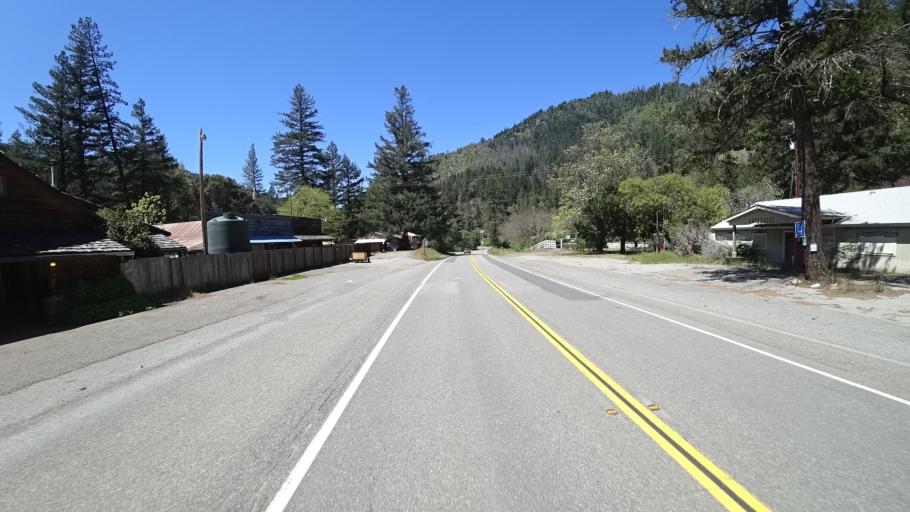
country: US
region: California
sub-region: Trinity County
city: Hayfork
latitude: 40.7446
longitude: -123.2685
